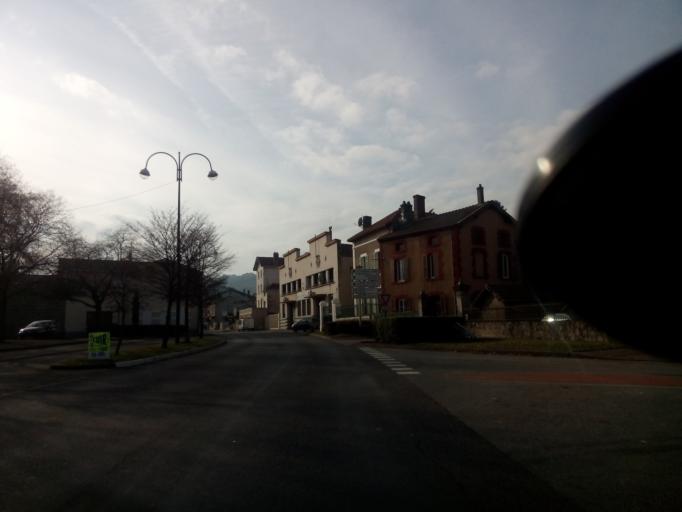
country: FR
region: Rhone-Alpes
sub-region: Departement de la Loire
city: Chavanay
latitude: 45.4180
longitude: 4.7378
